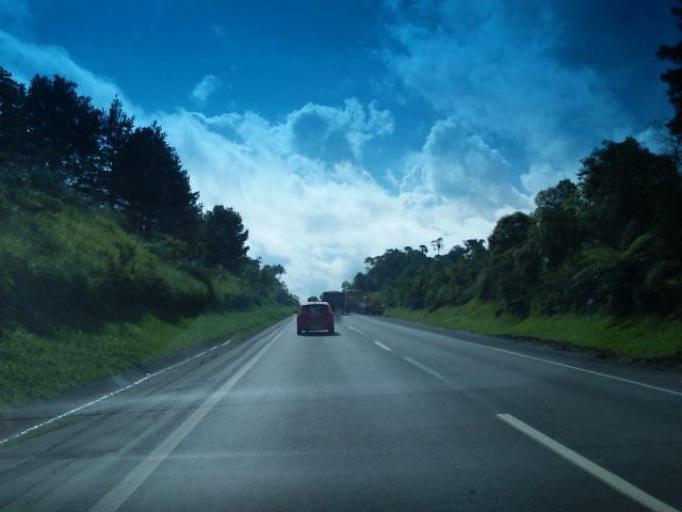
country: BR
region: Parana
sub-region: Antonina
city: Antonina
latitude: -25.1093
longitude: -48.7625
